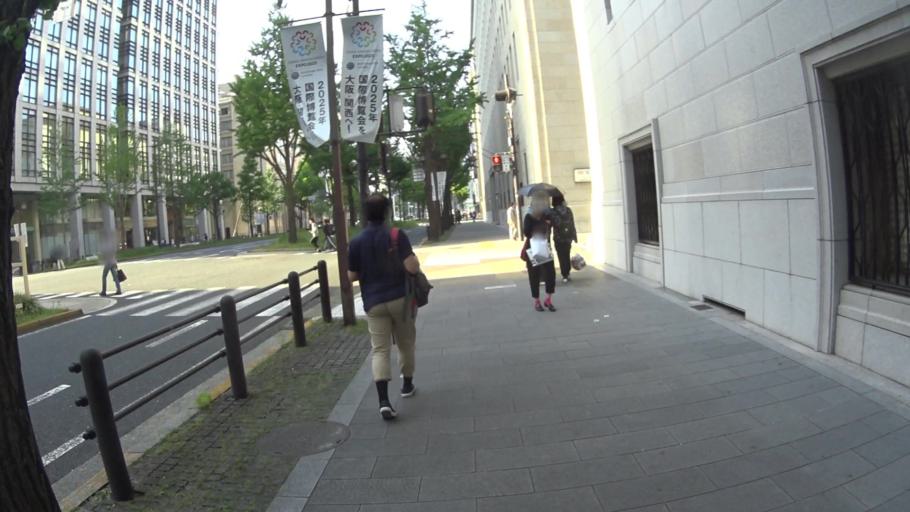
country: JP
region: Osaka
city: Osaka-shi
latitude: 34.6906
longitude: 135.5011
